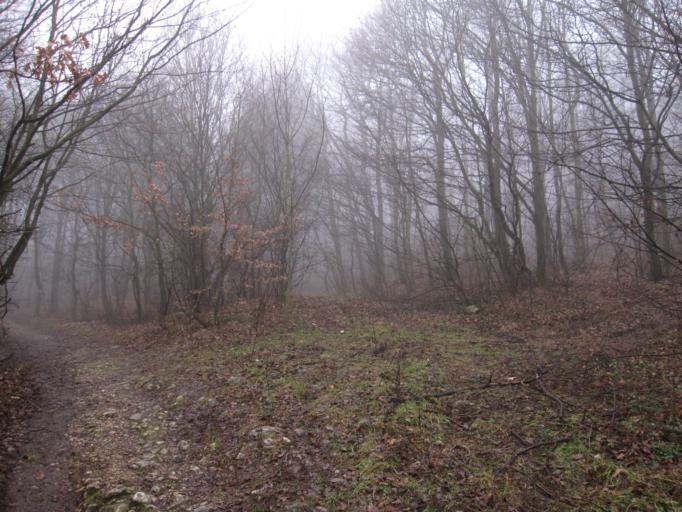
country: HU
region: Pest
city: Pilisszentivan
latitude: 47.5699
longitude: 18.8870
